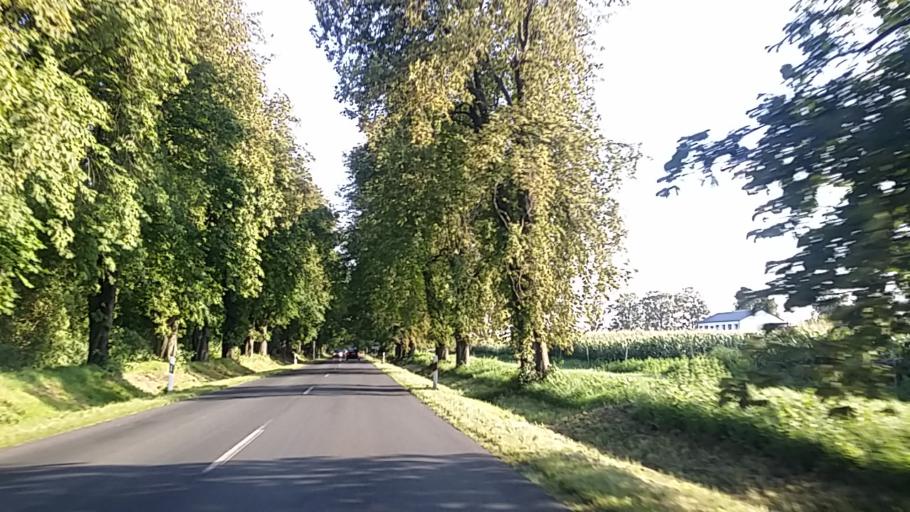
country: HU
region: Zala
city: Keszthely
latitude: 46.7369
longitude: 17.2403
